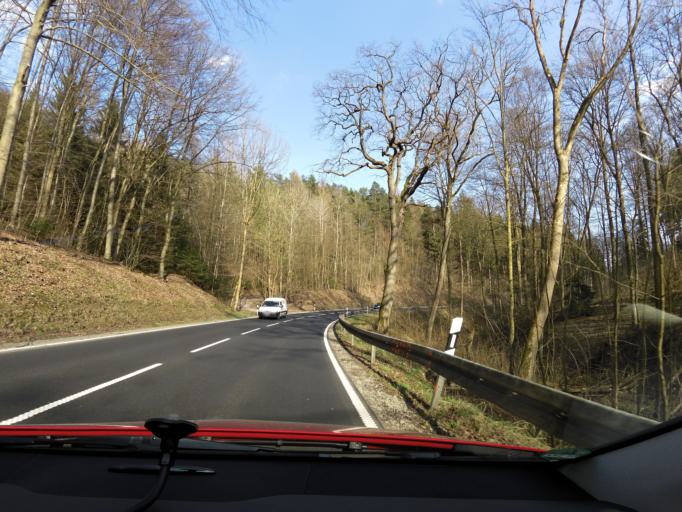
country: DE
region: Lower Saxony
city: Waake
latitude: 51.5822
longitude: 10.0764
